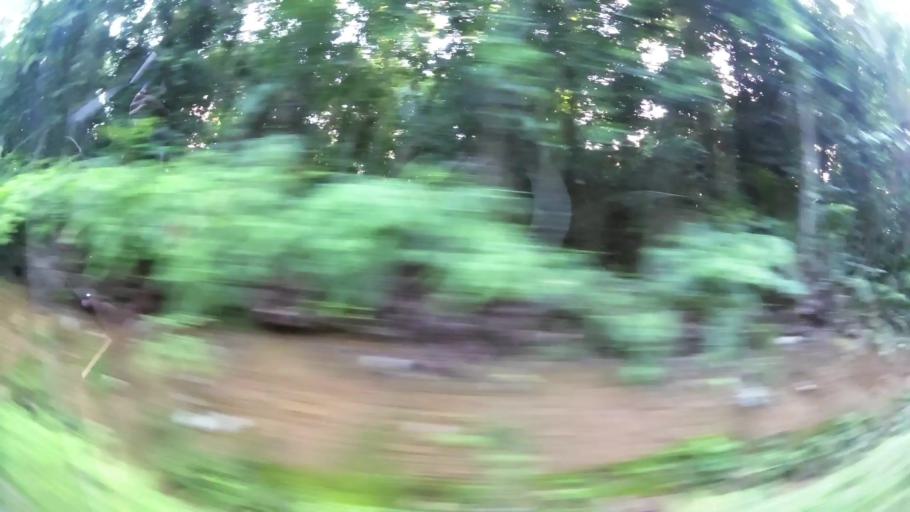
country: GP
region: Guadeloupe
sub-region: Guadeloupe
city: Petit-Bourg
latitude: 16.1821
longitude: -61.6816
